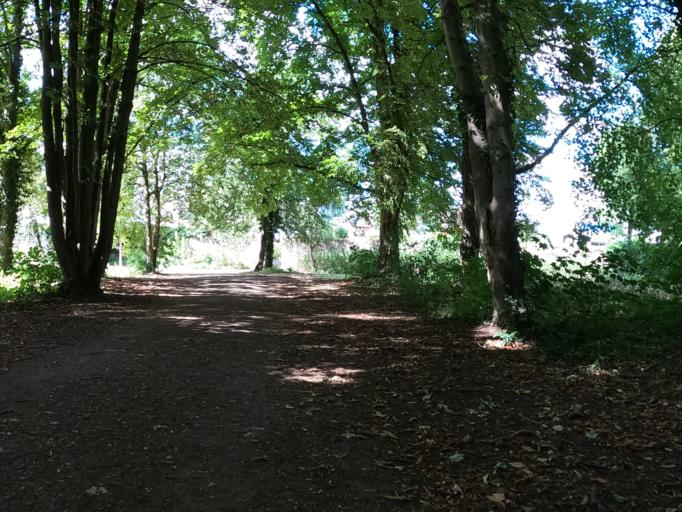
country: DE
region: Hesse
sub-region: Regierungsbezirk Darmstadt
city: Gross-Gerau
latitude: 49.9092
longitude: 8.4818
